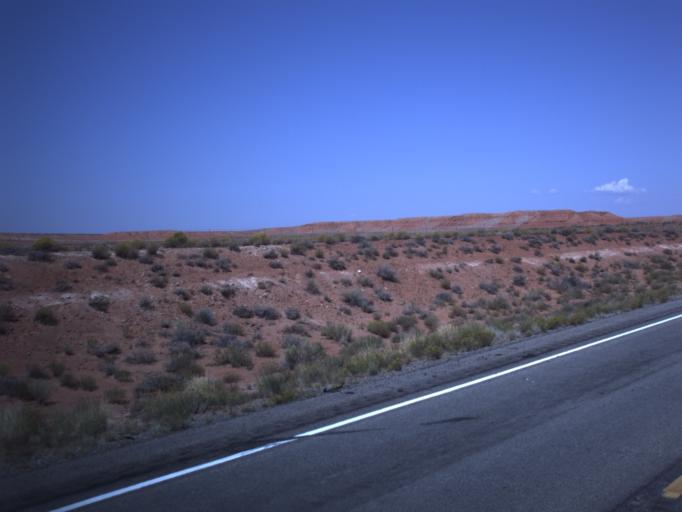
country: US
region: Utah
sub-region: San Juan County
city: Blanding
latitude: 36.9994
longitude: -109.6093
